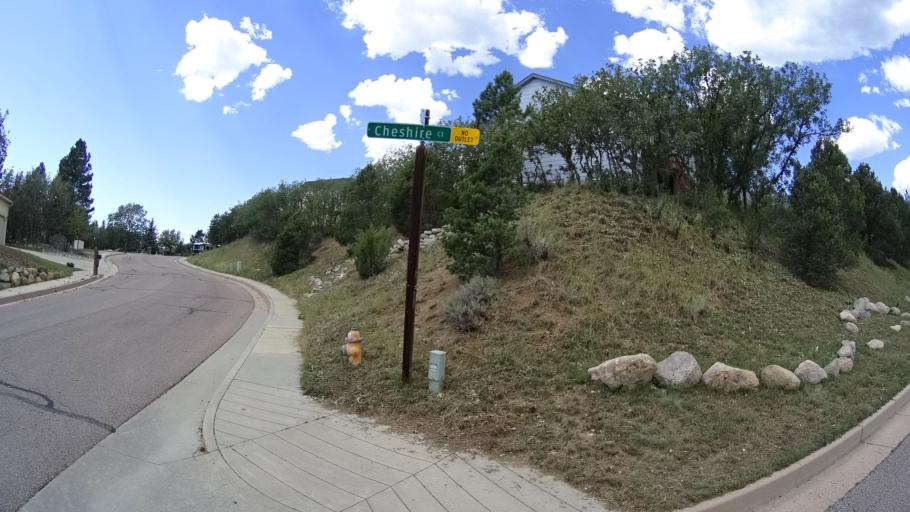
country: US
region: Colorado
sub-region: El Paso County
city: Fort Carson
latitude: 38.7632
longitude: -104.8231
